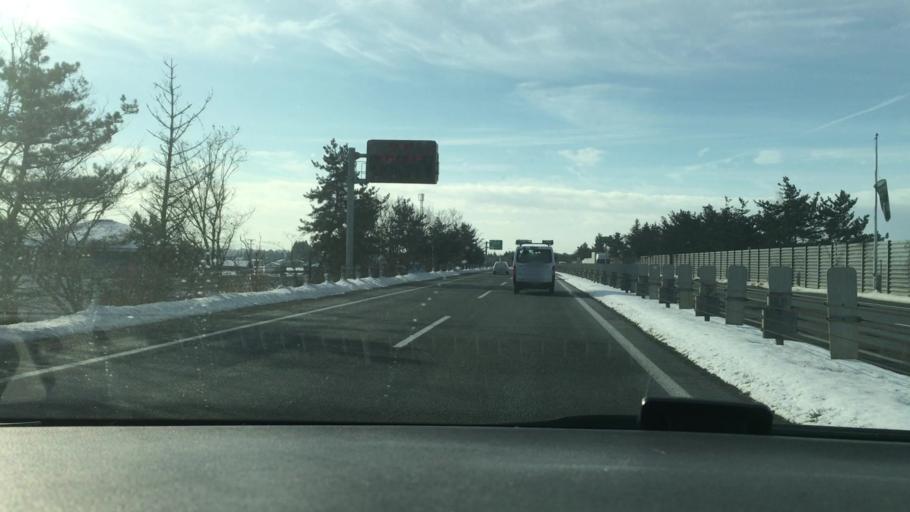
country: JP
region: Iwate
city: Hanamaki
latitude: 39.3920
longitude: 141.0920
